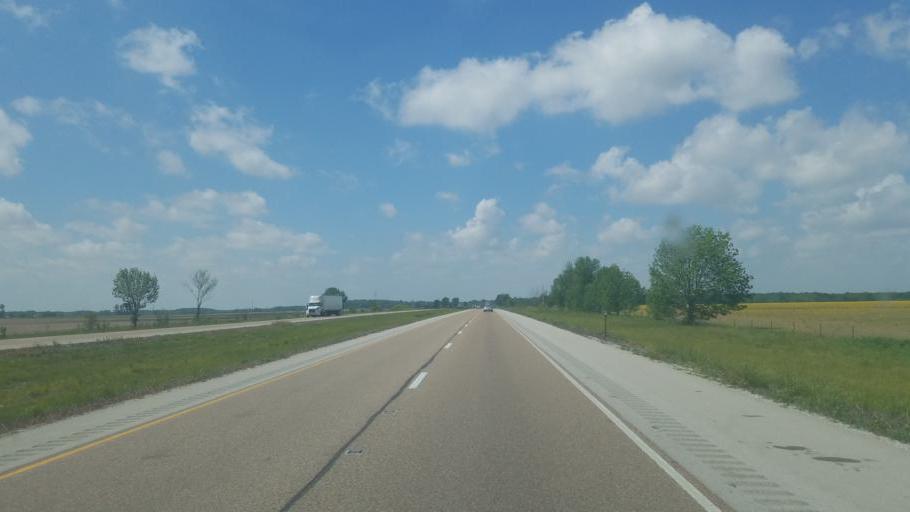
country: US
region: Illinois
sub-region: Clark County
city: Casey
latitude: 39.2965
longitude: -88.0319
